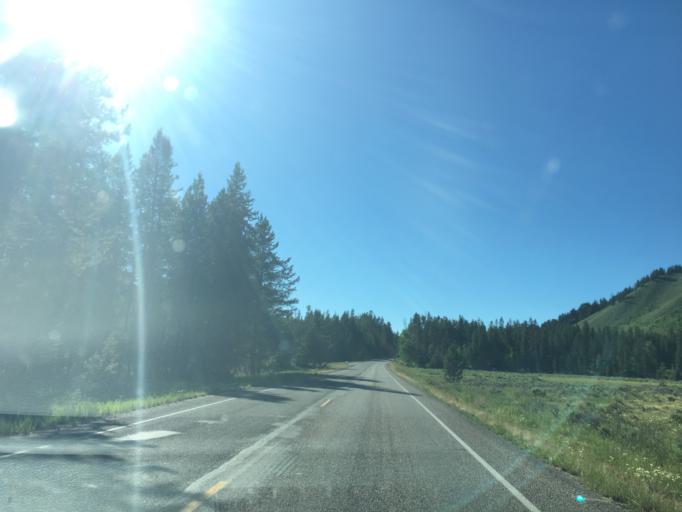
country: US
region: Wyoming
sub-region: Teton County
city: Jackson
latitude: 43.8550
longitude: -110.5221
